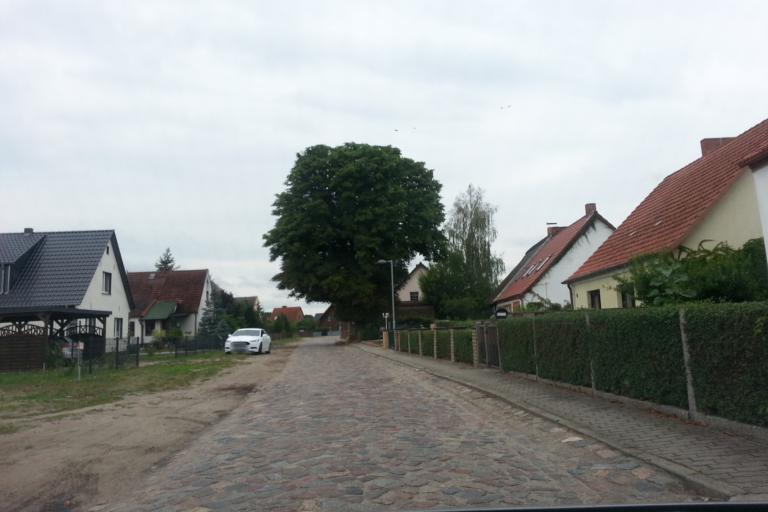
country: DE
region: Mecklenburg-Vorpommern
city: Ferdinandshof
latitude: 53.6949
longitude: 13.8892
